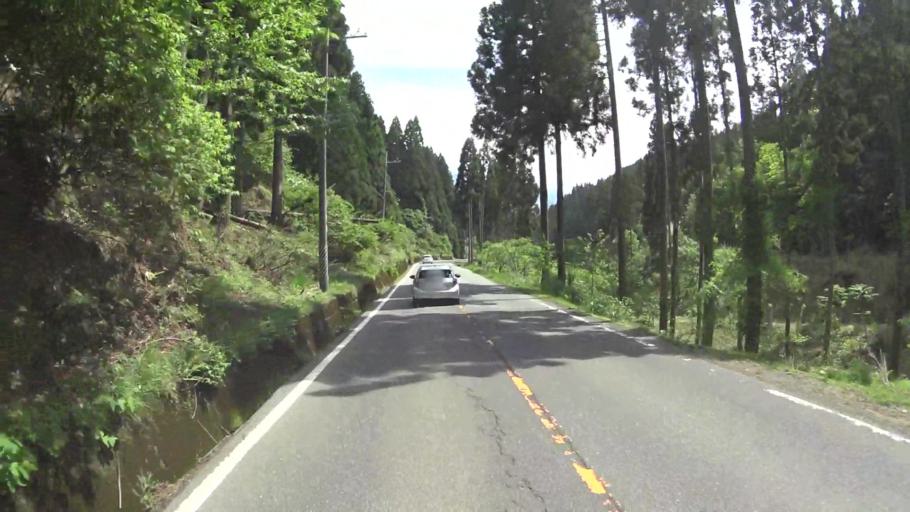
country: JP
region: Fukui
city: Obama
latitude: 35.3857
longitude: 135.9258
